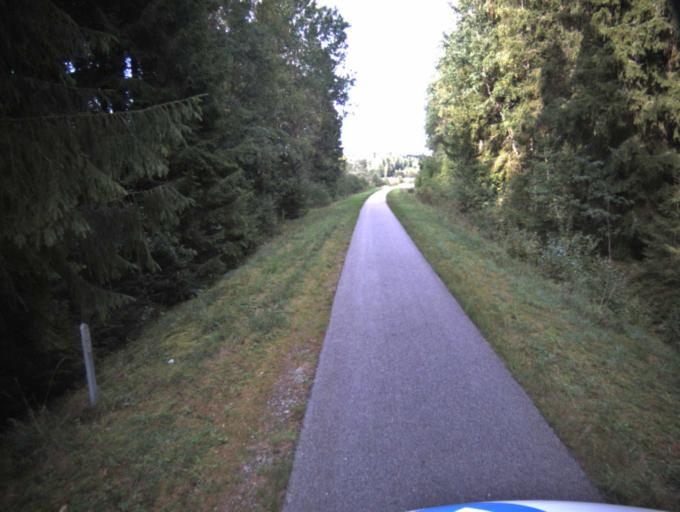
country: SE
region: Vaestra Goetaland
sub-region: Ulricehamns Kommun
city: Ulricehamn
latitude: 57.8746
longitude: 13.4279
